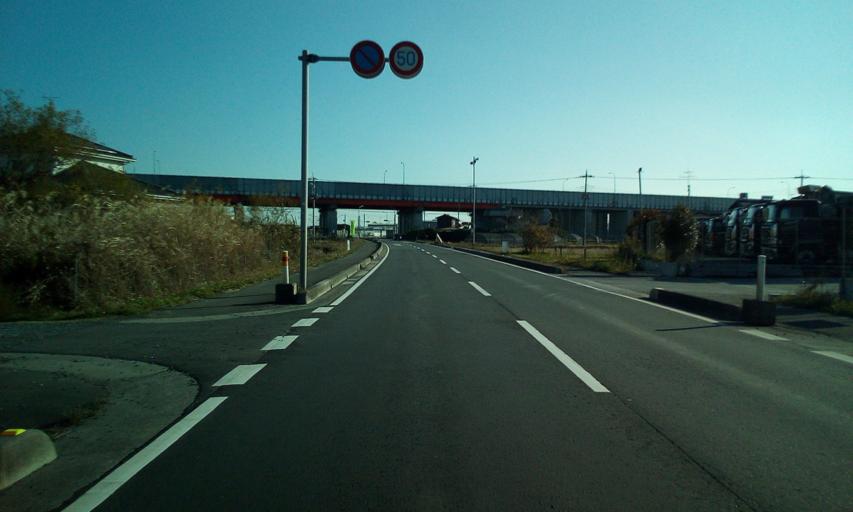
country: JP
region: Chiba
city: Nagareyama
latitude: 35.8752
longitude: 139.8892
